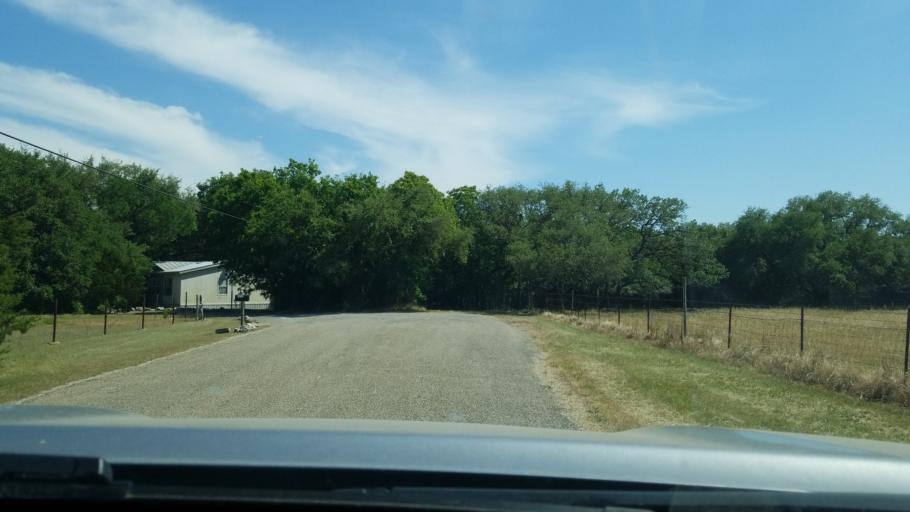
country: US
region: Texas
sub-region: Bexar County
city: Timberwood Park
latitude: 29.7452
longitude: -98.5154
